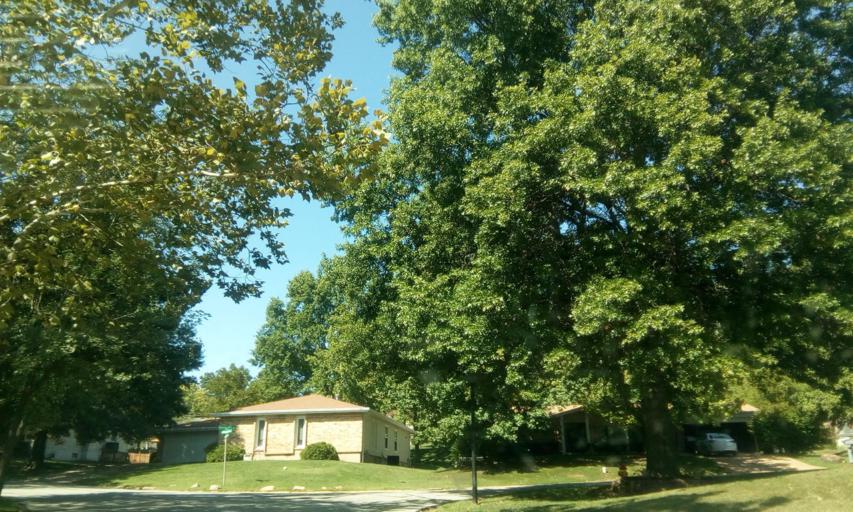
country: US
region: Missouri
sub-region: Saint Louis County
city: Ballwin
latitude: 38.5993
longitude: -90.5471
